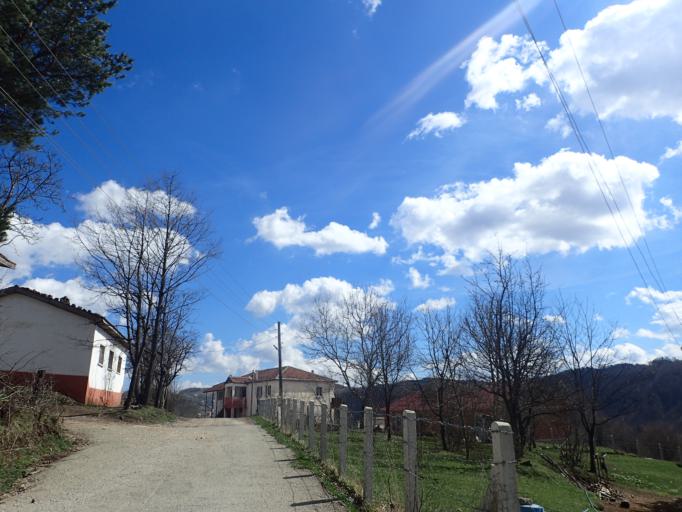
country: TR
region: Ordu
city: Kumru
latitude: 40.8054
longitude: 37.1876
